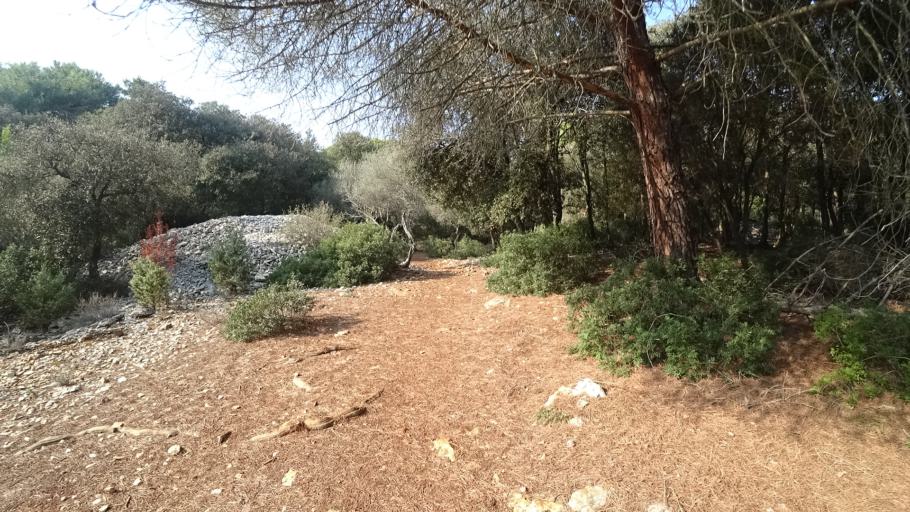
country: HR
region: Primorsko-Goranska
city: Mali Losinj
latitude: 44.4952
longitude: 14.5030
